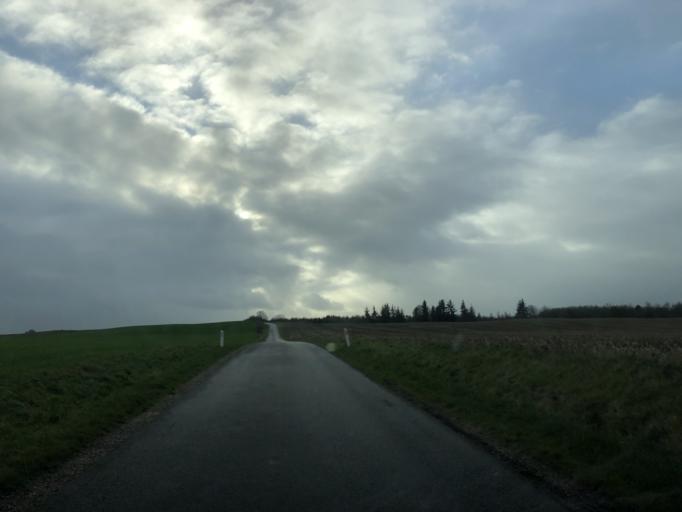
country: DK
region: North Denmark
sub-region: Rebild Kommune
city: Stovring
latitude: 56.9161
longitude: 9.7813
